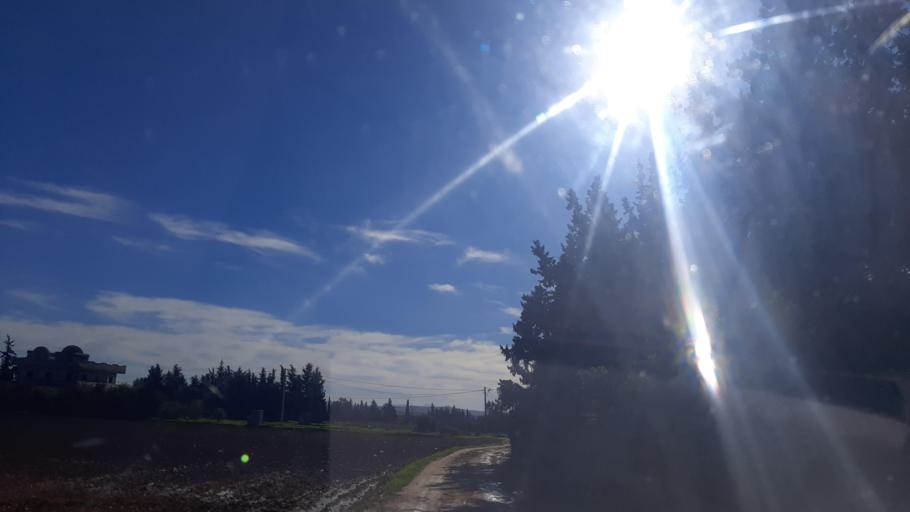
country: TN
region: Tunis
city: Oued Lill
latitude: 36.7593
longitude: 9.9819
